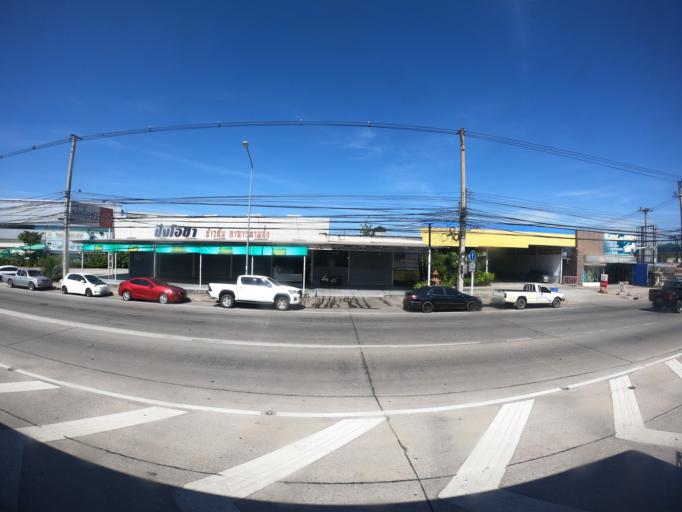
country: TH
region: Nakhon Ratchasima
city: Nakhon Ratchasima
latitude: 14.9890
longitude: 102.0963
